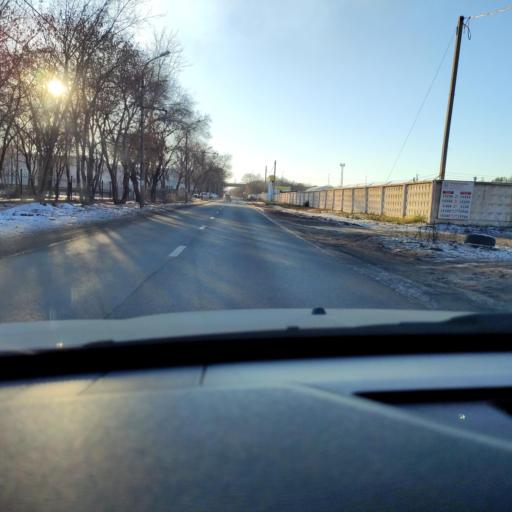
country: RU
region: Samara
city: Samara
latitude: 53.1167
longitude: 50.0676
